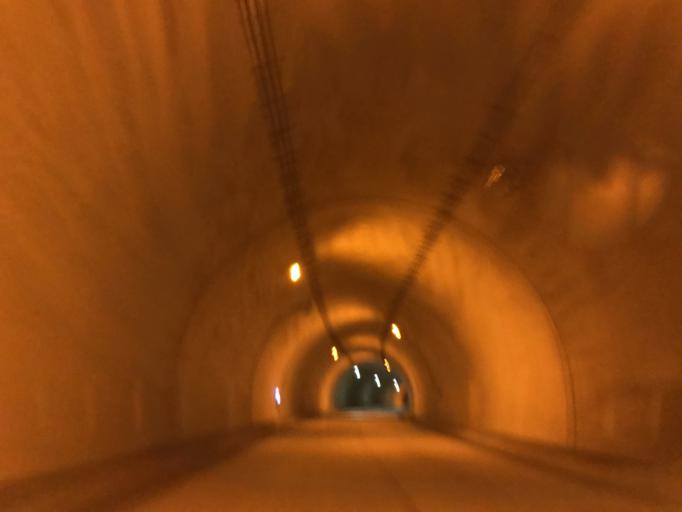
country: JP
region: Iwate
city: Mizusawa
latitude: 39.0260
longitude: 141.0190
